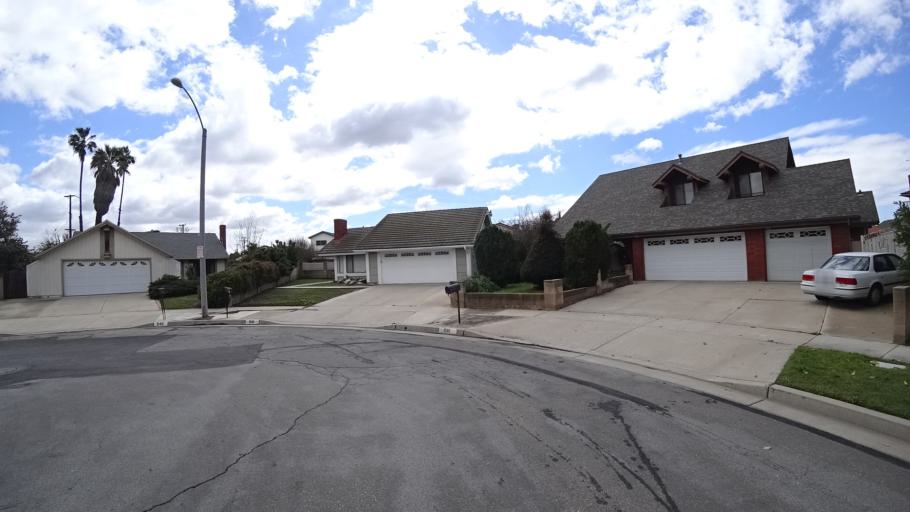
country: US
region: California
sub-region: Orange County
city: Anaheim
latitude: 33.8255
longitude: -117.9353
